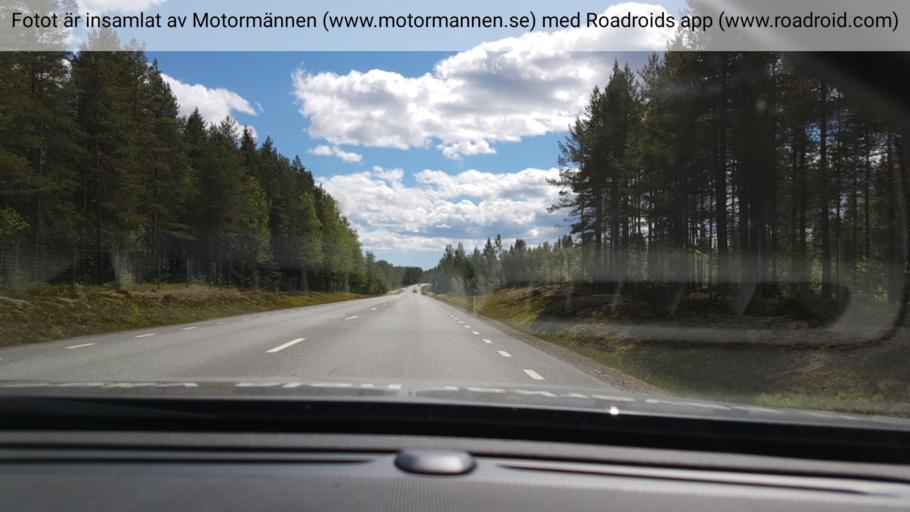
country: SE
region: Vaesterbotten
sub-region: Robertsfors Kommun
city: Robertsfors
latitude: 64.0508
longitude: 20.8482
